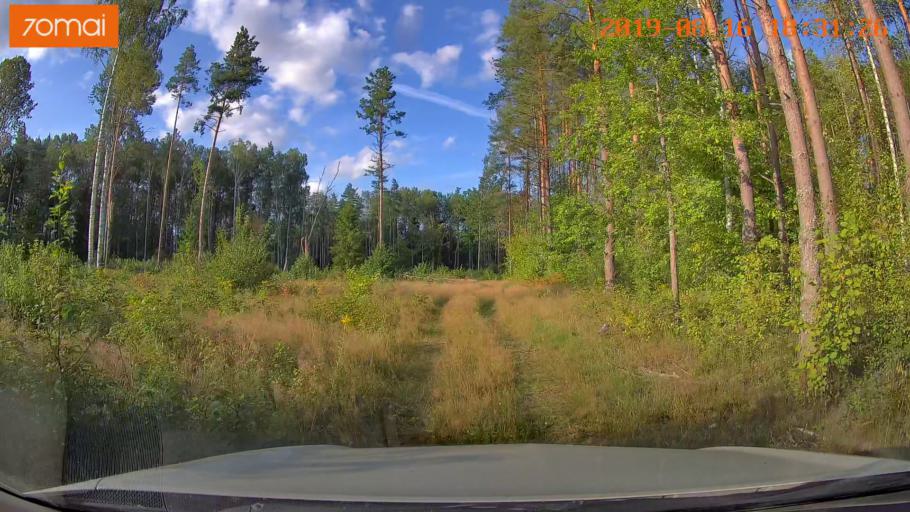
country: BY
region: Mogilev
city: Asipovichy
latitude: 53.1977
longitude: 28.6387
